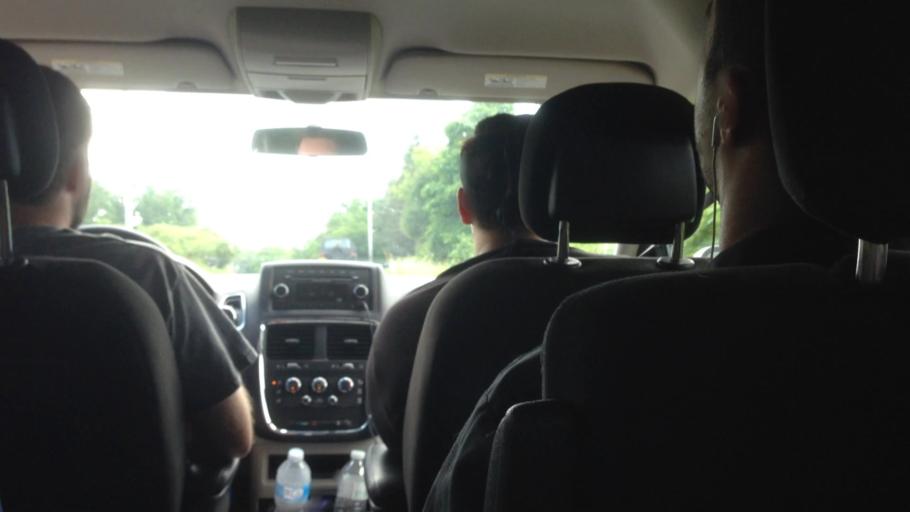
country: US
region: New York
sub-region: Dutchess County
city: Tivoli
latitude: 42.0503
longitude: -73.8976
